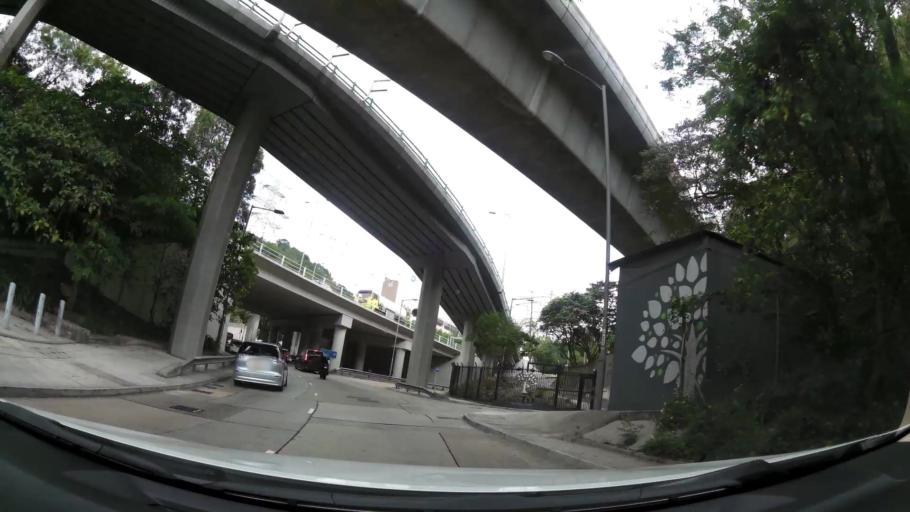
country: HK
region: Sham Shui Po
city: Sham Shui Po
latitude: 22.3398
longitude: 114.1419
